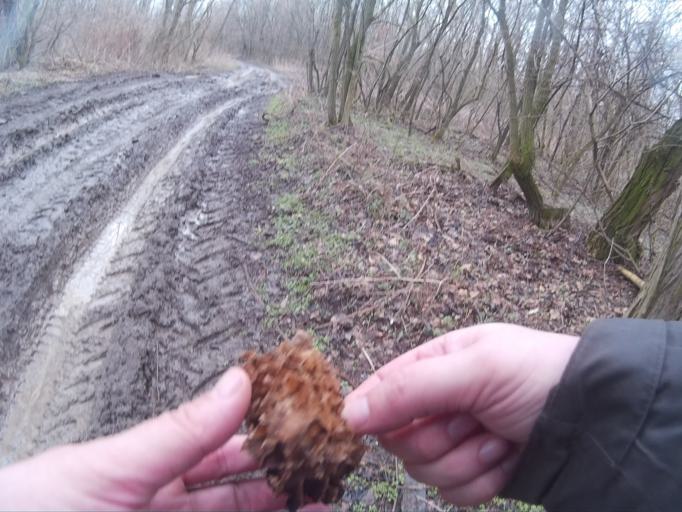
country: HU
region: Komarom-Esztergom
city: Tarjan
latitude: 47.5608
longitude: 18.5528
